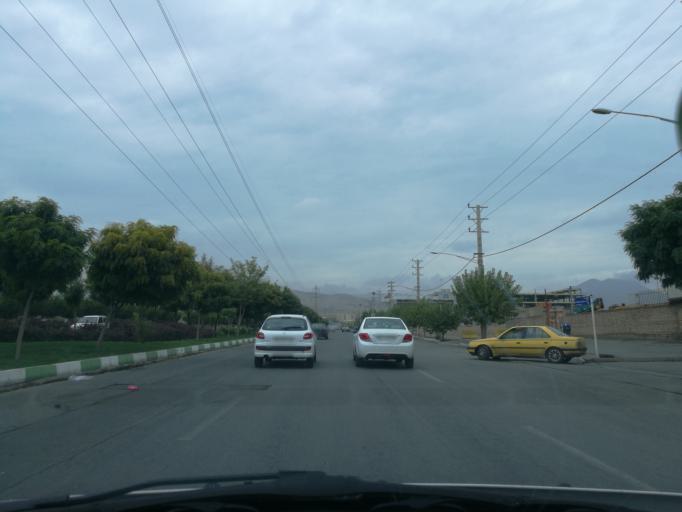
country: IR
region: Alborz
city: Karaj
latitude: 35.8545
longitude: 50.9205
